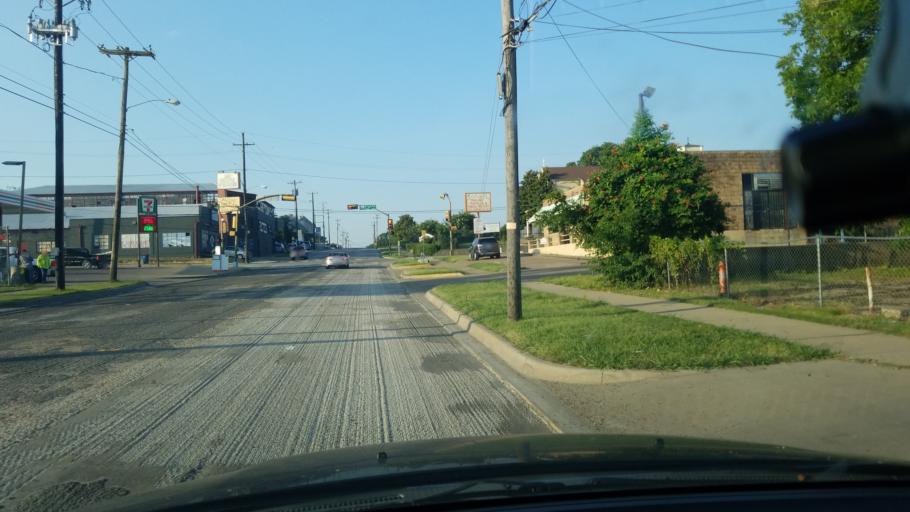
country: US
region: Texas
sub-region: Dallas County
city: Dallas
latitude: 32.7519
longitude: -96.8157
